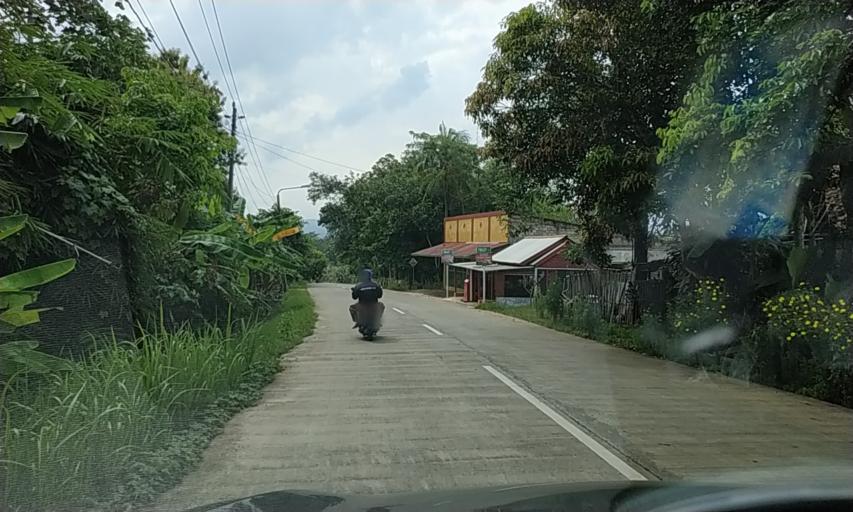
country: ID
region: Central Java
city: Winangun
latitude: -7.3635
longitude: 108.7014
